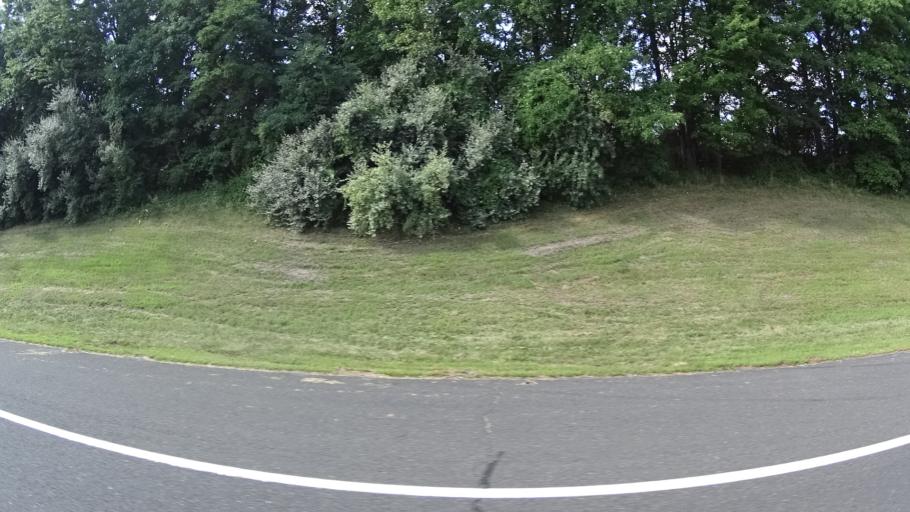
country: US
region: New Jersey
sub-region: Monmouth County
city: Strathmore
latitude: 40.4016
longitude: -74.1926
